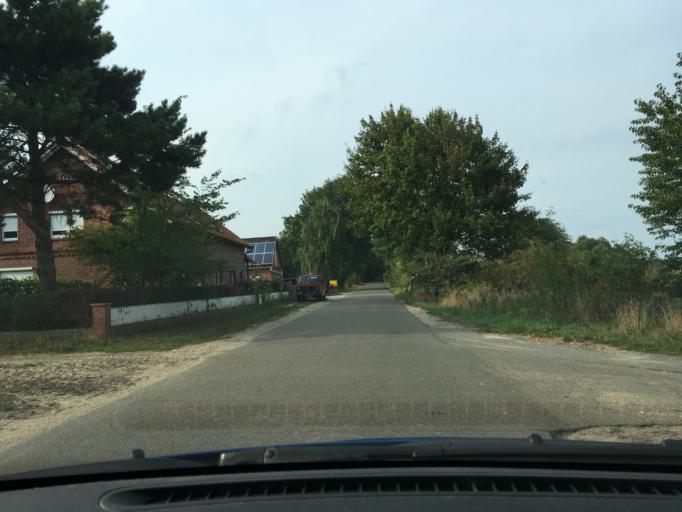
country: DE
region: Lower Saxony
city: Toppenstedt
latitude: 53.3026
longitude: 10.0967
